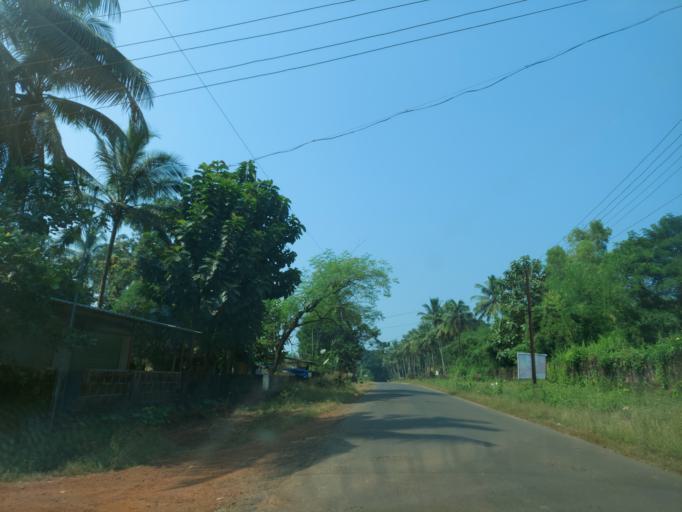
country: IN
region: Maharashtra
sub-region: Sindhudurg
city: Kudal
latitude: 15.9884
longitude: 73.6770
